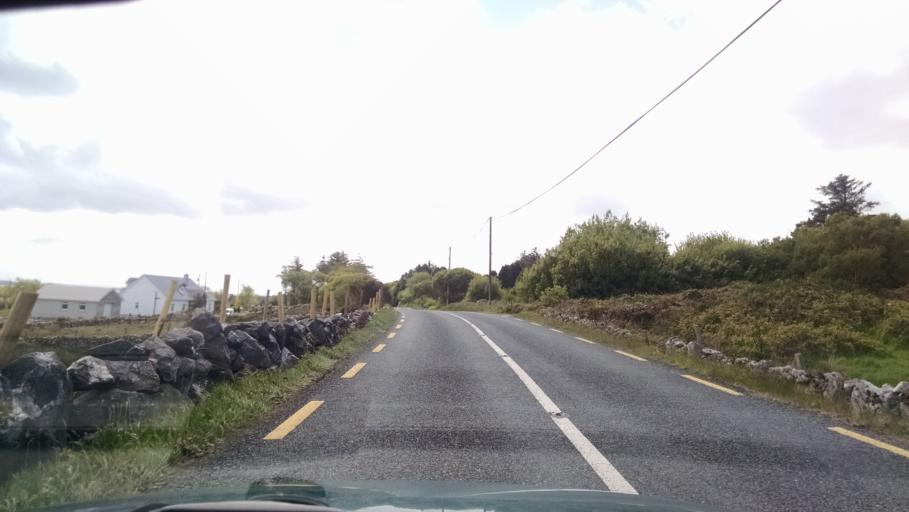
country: IE
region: Connaught
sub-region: County Galway
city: Clifden
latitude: 53.3492
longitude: -9.7085
